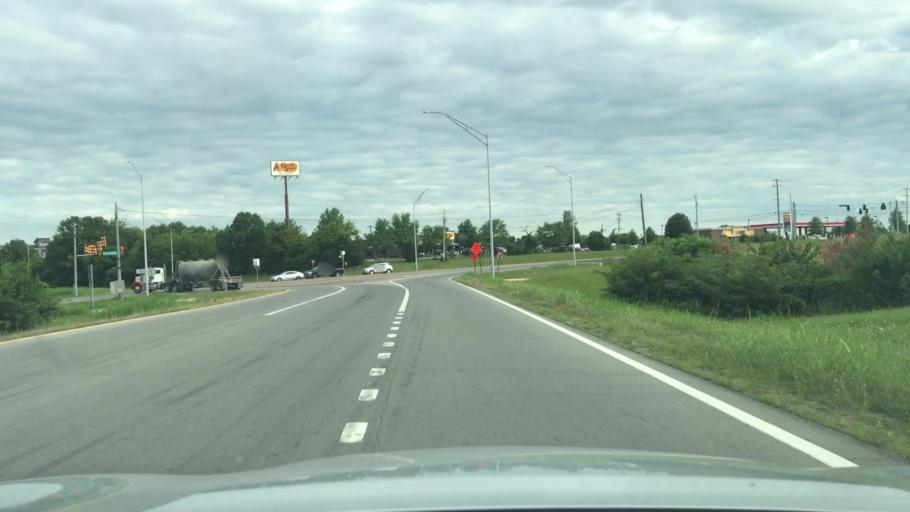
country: US
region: Tennessee
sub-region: Montgomery County
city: Clarksville
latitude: 36.6004
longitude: -87.2805
